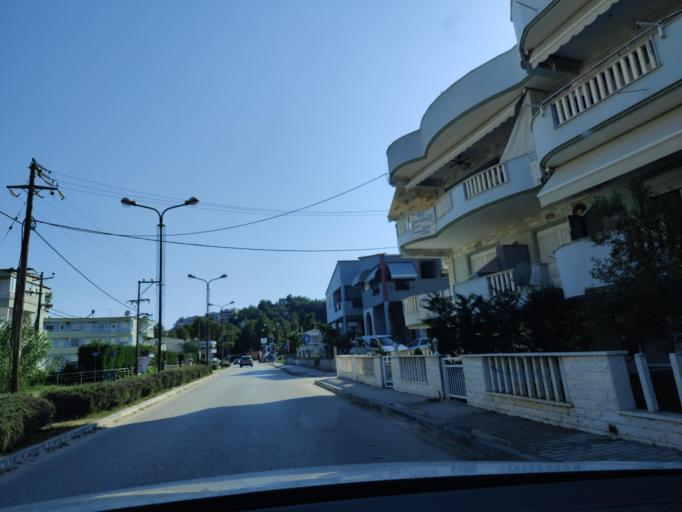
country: GR
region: East Macedonia and Thrace
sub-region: Nomos Kavalas
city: Nea Peramos
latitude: 40.8469
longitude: 24.3077
